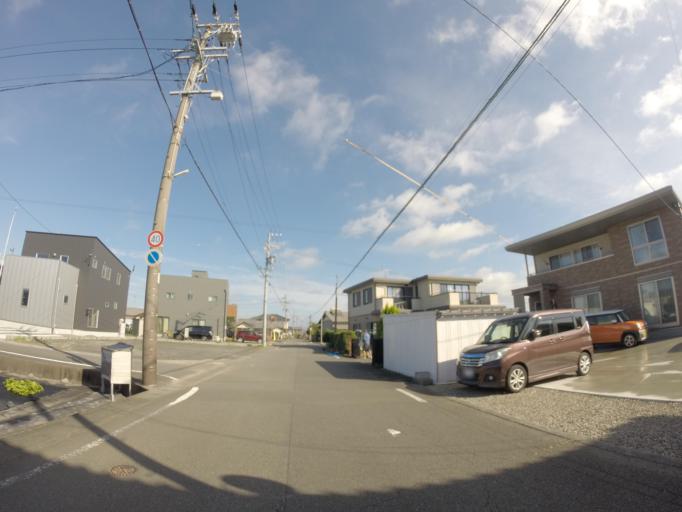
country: JP
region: Shizuoka
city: Fujieda
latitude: 34.7845
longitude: 138.2843
